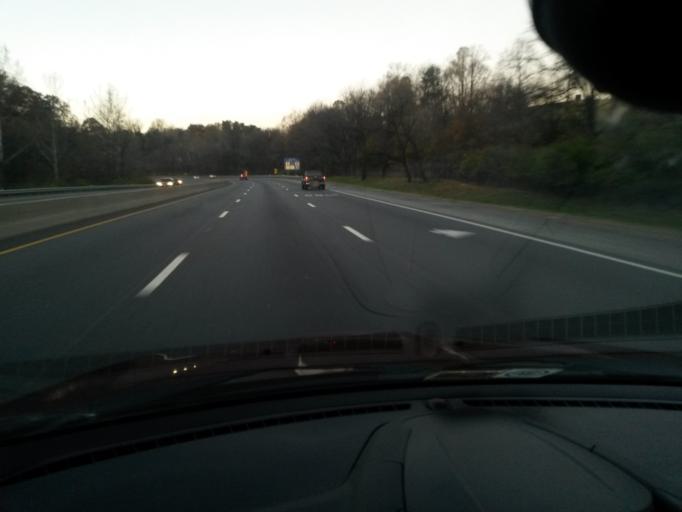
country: US
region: Virginia
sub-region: City of Roanoke
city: Roanoke
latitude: 37.2452
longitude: -79.9693
